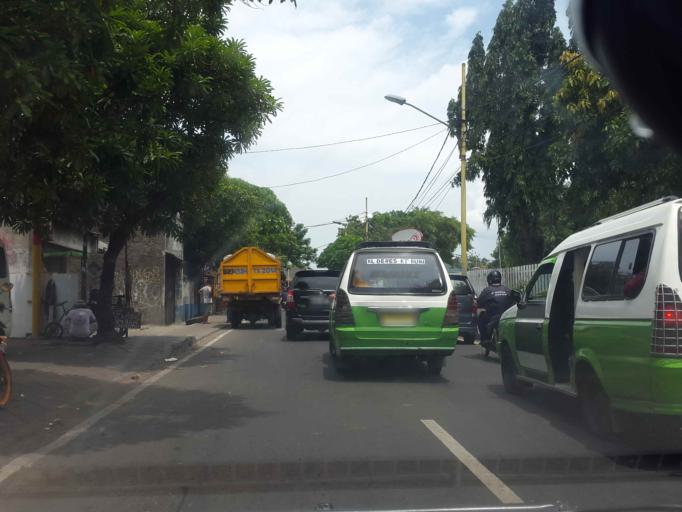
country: ID
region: Banten
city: Tangerang
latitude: -6.1694
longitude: 106.6261
